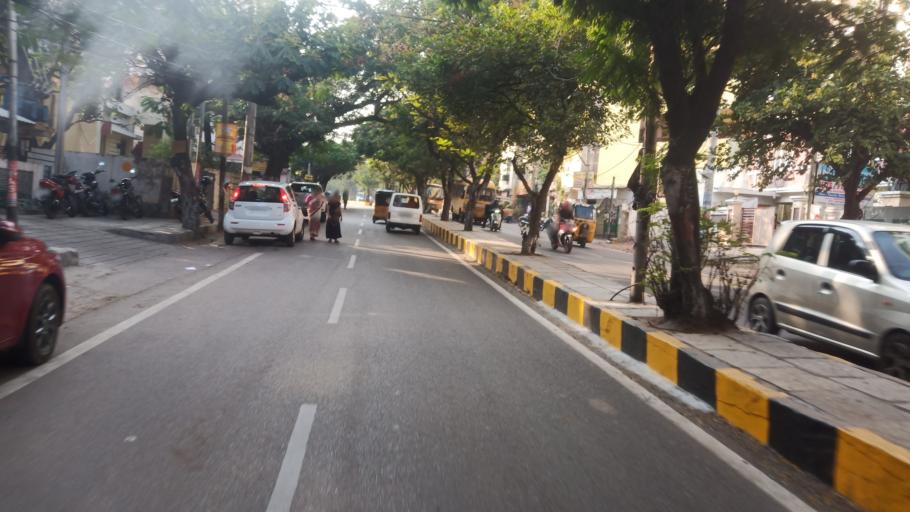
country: IN
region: Telangana
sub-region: Rangareddi
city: Kukatpalli
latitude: 17.4425
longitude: 78.4388
